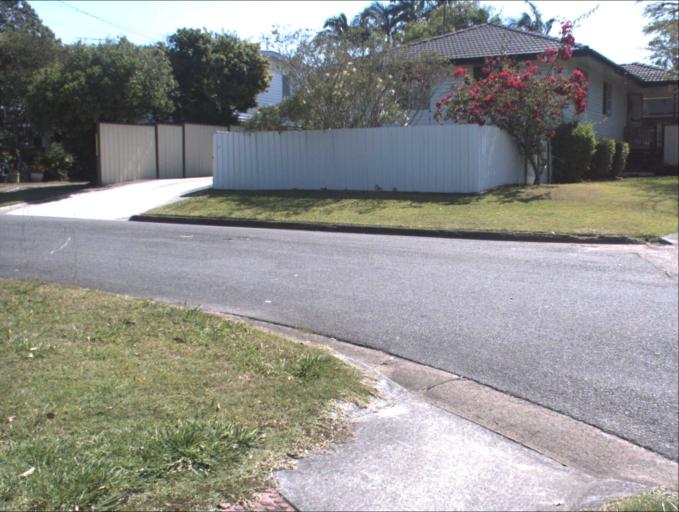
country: AU
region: Queensland
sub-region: Logan
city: Logan City
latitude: -27.6580
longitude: 153.1136
